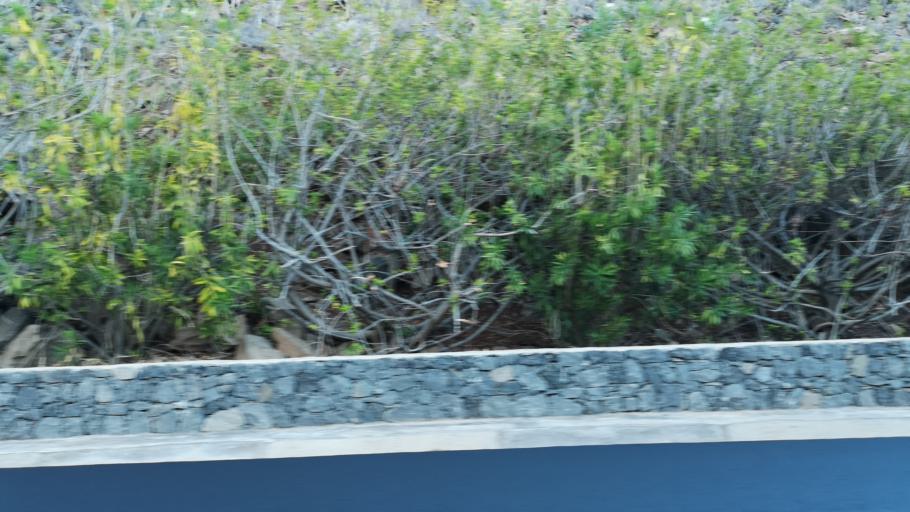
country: ES
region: Canary Islands
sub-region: Provincia de Santa Cruz de Tenerife
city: Alajero
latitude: 28.0344
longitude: -17.2039
